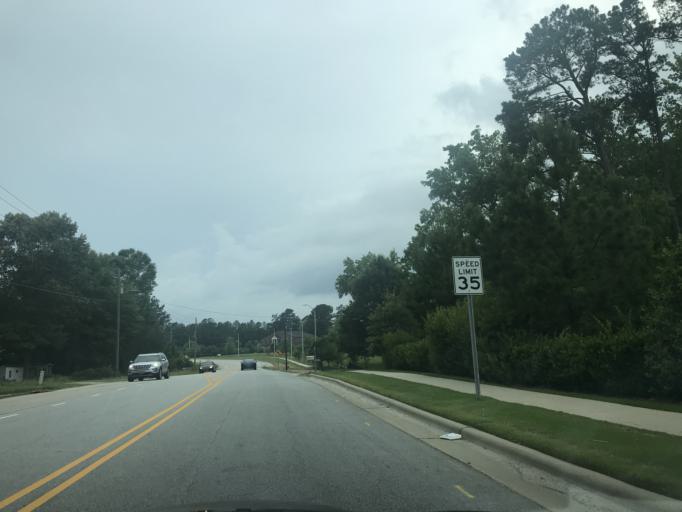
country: US
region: North Carolina
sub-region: Wake County
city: Green Level
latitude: 35.8056
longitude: -78.8864
